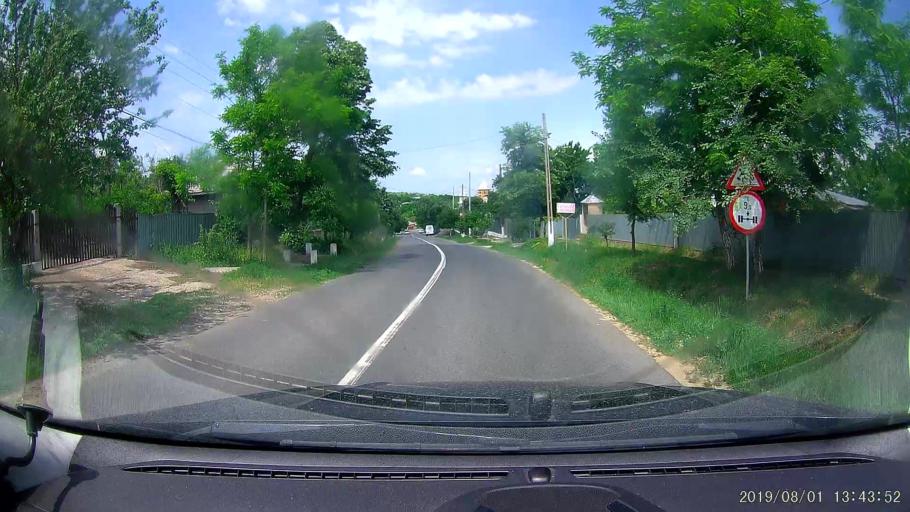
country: RO
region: Galati
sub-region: Comuna Oancea
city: Oancea
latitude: 45.9175
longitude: 28.1133
